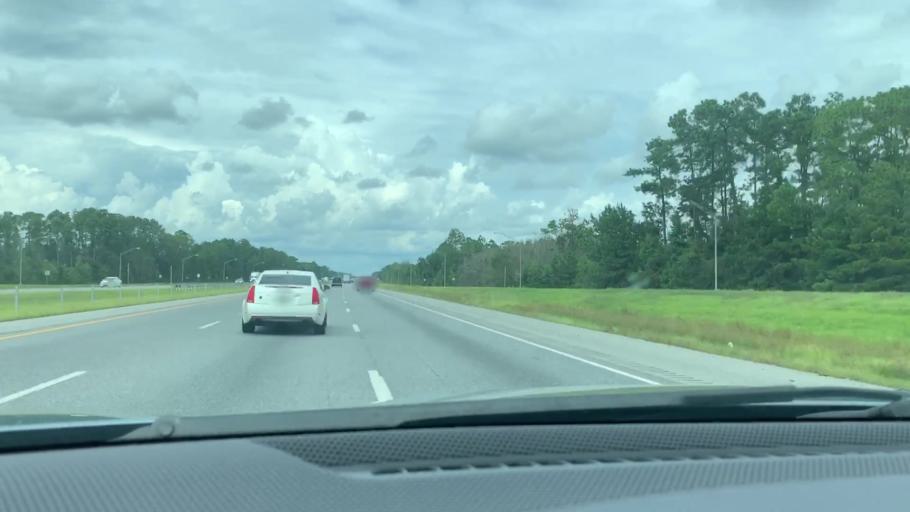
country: US
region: Georgia
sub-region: McIntosh County
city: Darien
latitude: 31.4793
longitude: -81.4470
